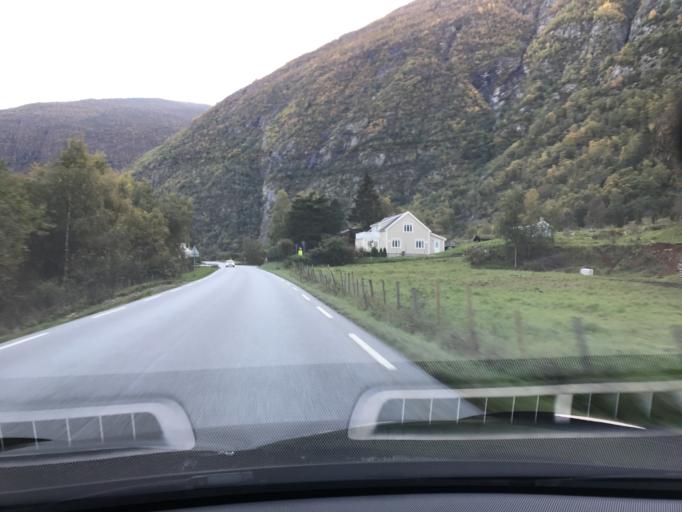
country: NO
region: Sogn og Fjordane
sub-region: Laerdal
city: Laerdalsoyri
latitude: 61.0768
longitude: 7.5023
